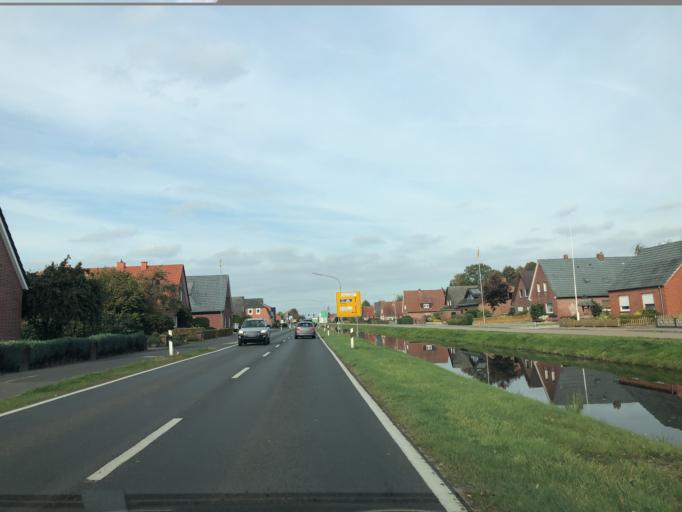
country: DE
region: Lower Saxony
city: Papenburg
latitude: 53.0603
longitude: 7.4522
